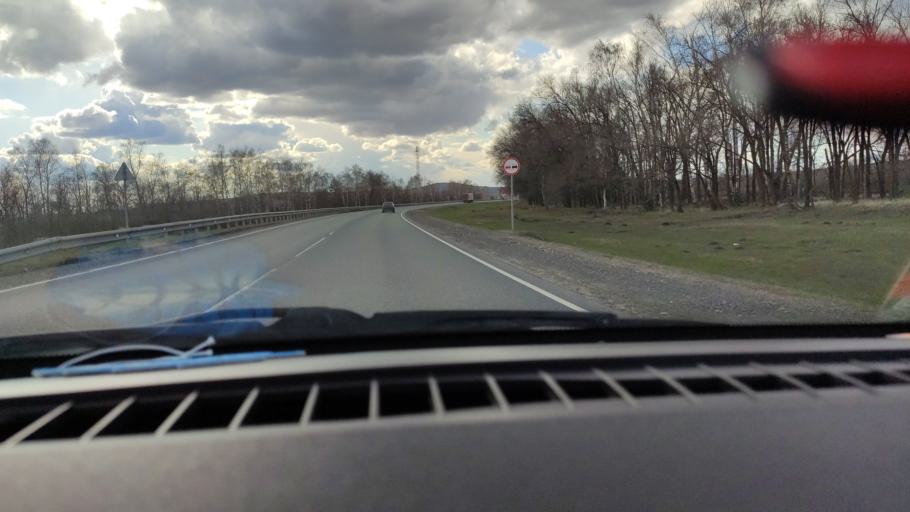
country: RU
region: Saratov
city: Tersa
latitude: 52.0832
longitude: 47.5569
